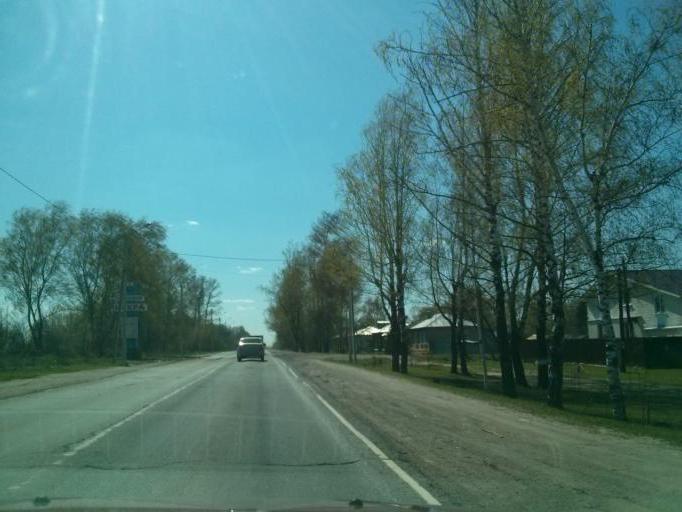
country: RU
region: Nizjnij Novgorod
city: Bogorodsk
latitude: 56.0627
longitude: 43.4221
